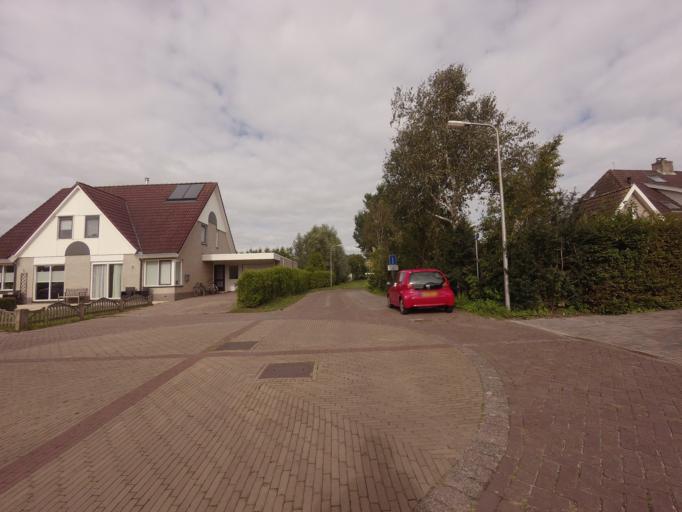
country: NL
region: Friesland
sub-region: Sudwest Fryslan
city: Workum
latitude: 52.9791
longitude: 5.4515
